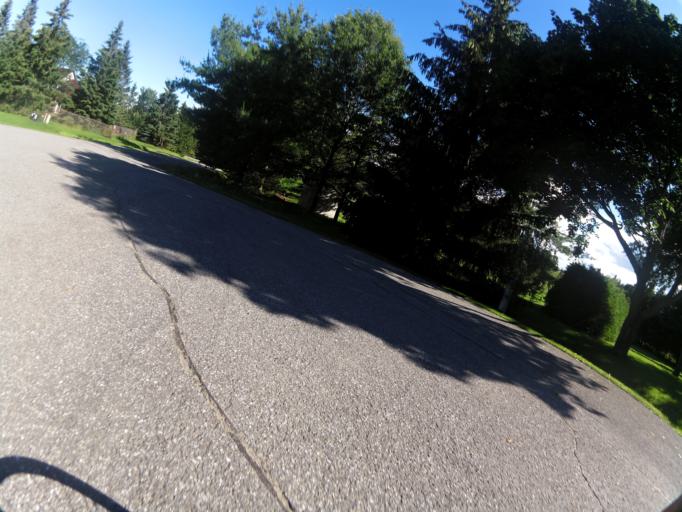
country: CA
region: Ontario
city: Bells Corners
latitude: 45.2640
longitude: -75.8231
